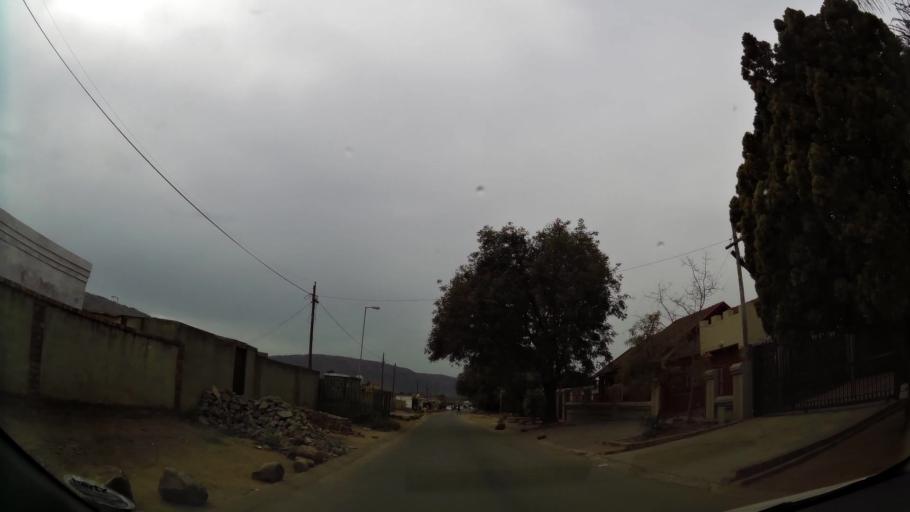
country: ZA
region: Gauteng
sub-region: City of Tshwane Metropolitan Municipality
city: Pretoria
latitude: -25.7094
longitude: 28.3475
